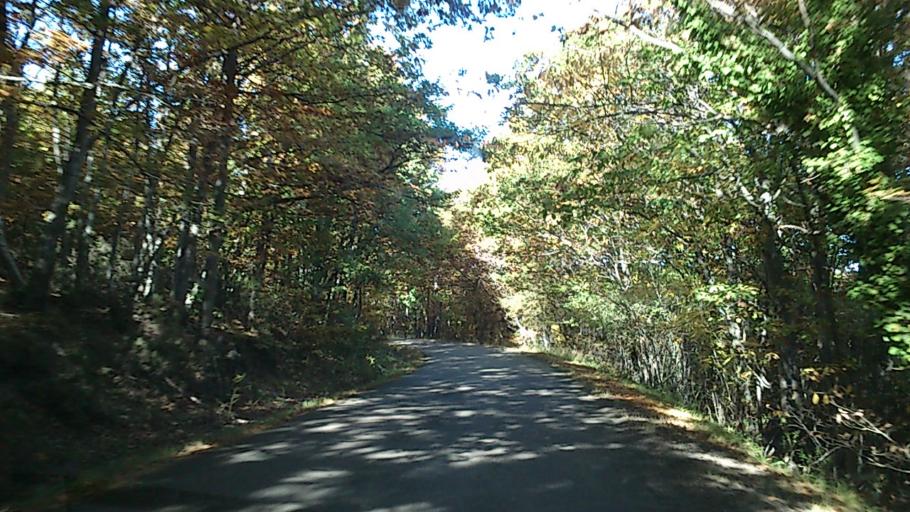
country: ES
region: Aragon
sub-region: Provincia de Zaragoza
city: Litago
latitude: 41.7969
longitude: -1.7868
